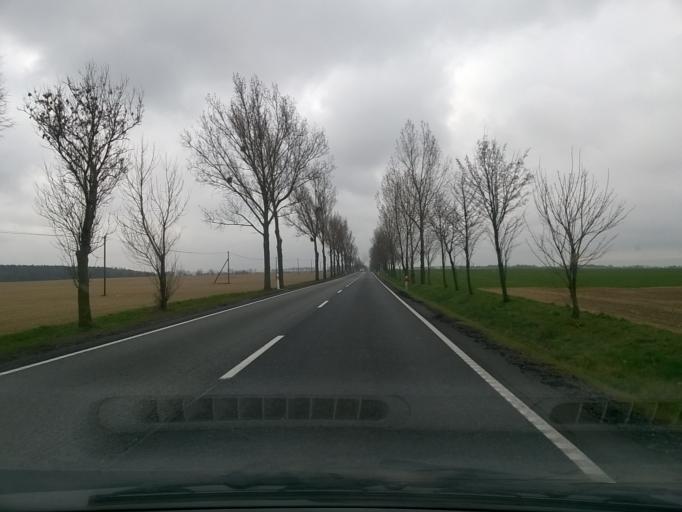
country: PL
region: Kujawsko-Pomorskie
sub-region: Powiat zninski
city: Znin
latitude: 52.9050
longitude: 17.7005
